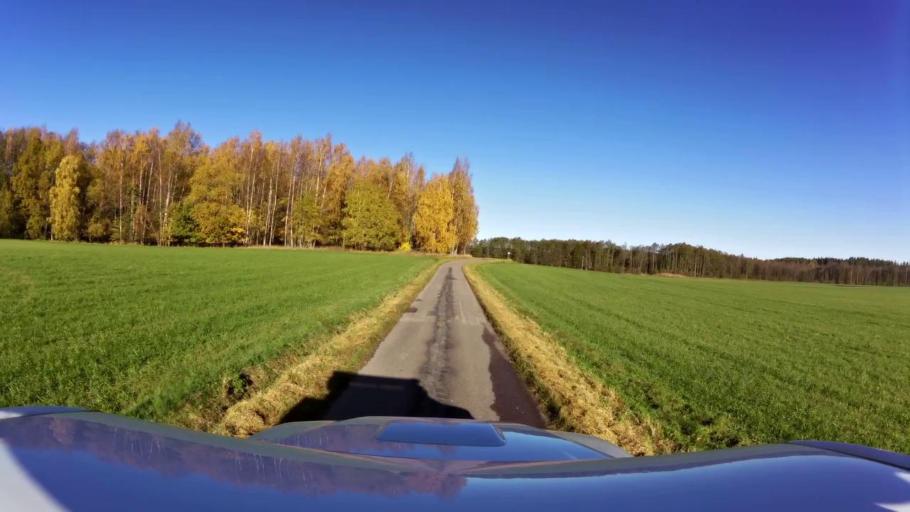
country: SE
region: OEstergoetland
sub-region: Motala Kommun
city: Borensberg
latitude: 58.5394
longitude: 15.3883
